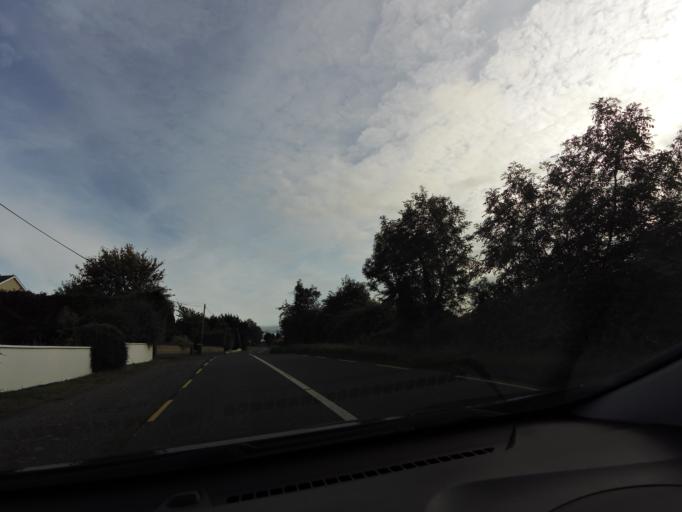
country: IE
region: Connaught
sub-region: County Galway
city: Ballinasloe
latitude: 53.3130
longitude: -8.2803
